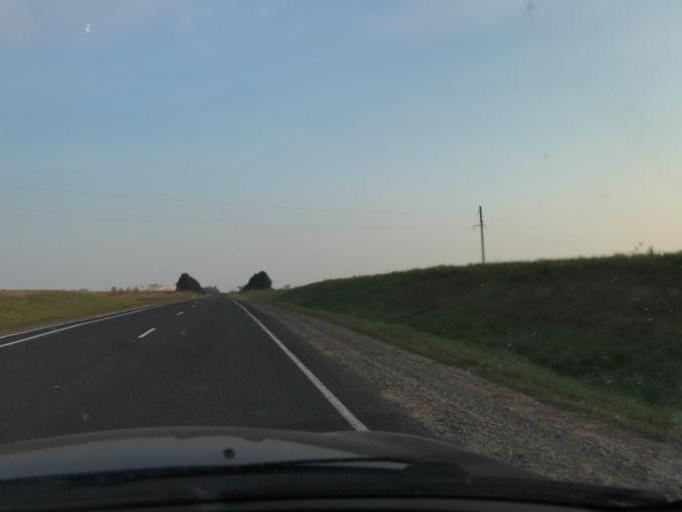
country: BY
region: Grodnenskaya
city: Karelichy
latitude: 53.5823
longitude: 26.1177
